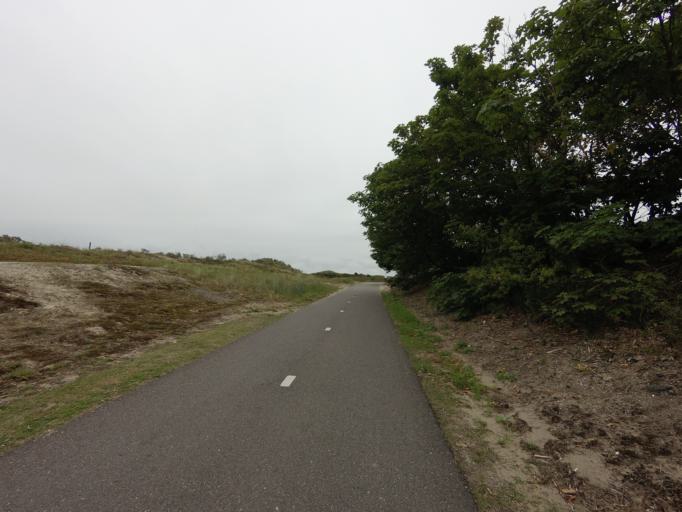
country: NL
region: South Holland
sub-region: Gemeente Katwijk
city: Katwijk aan Zee
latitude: 52.1753
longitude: 4.3691
